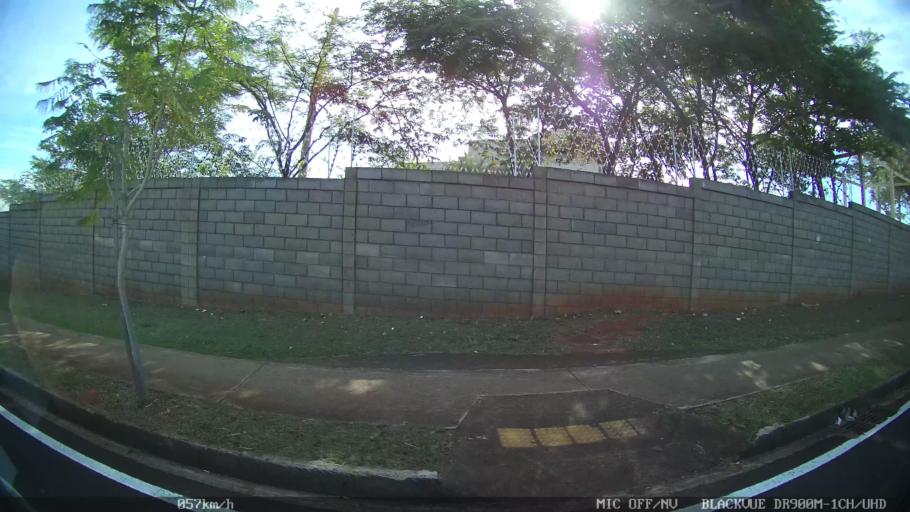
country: BR
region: Sao Paulo
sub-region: Sao Jose Do Rio Preto
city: Sao Jose do Rio Preto
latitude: -20.8101
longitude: -49.3350
